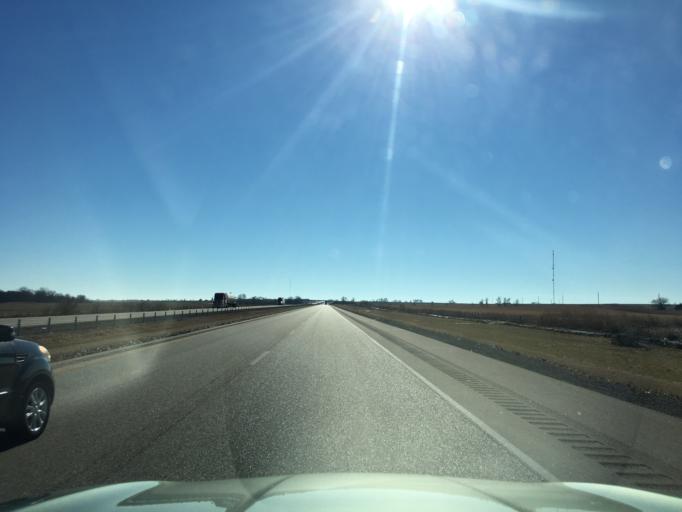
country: US
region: Oklahoma
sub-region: Kay County
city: Blackwell
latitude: 36.8923
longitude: -97.3537
